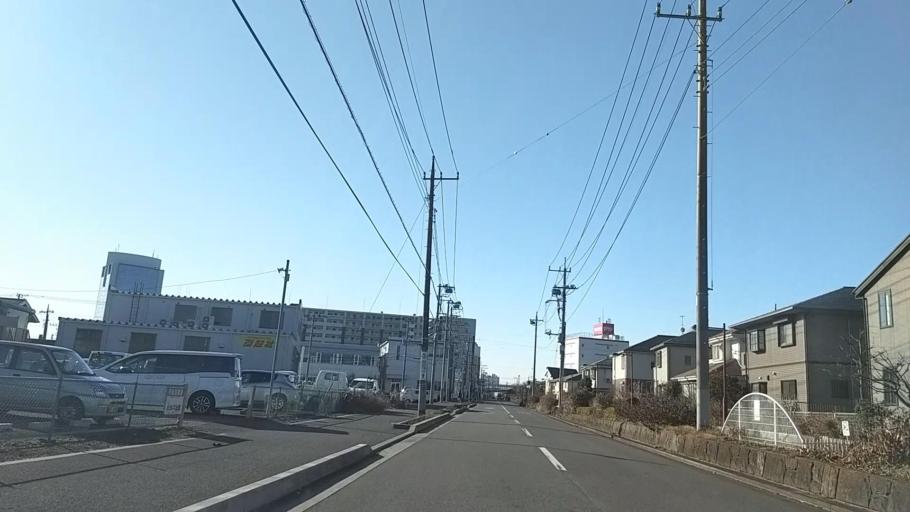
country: JP
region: Kanagawa
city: Atsugi
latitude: 35.4299
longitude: 139.3593
